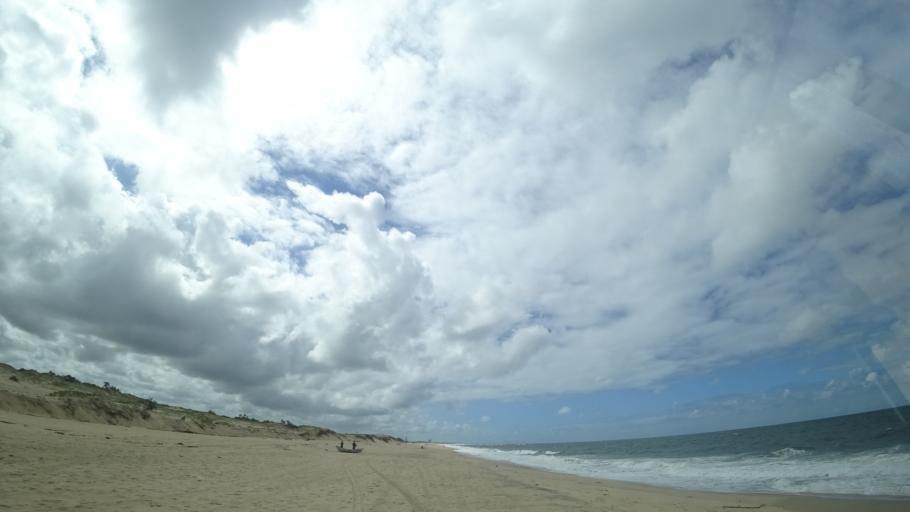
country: MZ
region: Sofala
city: Beira
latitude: -19.6157
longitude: 35.2205
